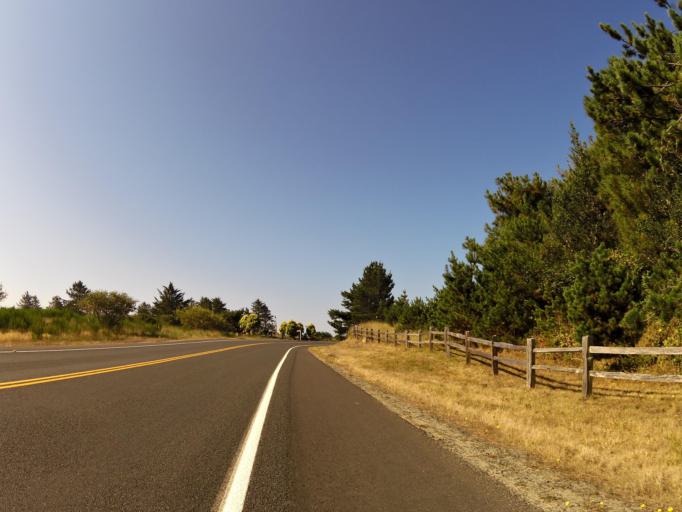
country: US
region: Oregon
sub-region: Clatsop County
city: Gearhart
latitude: 46.0493
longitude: -123.9218
